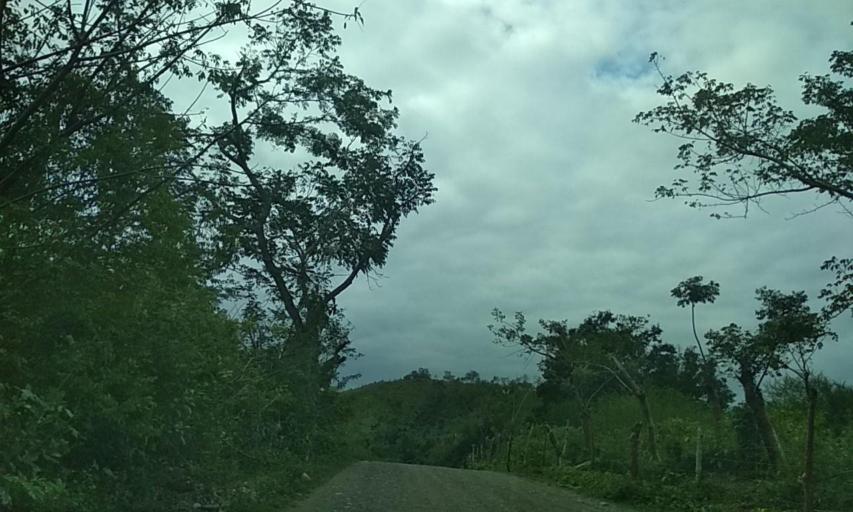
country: MX
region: Veracruz
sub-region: Papantla
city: Residencial Tajin
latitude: 20.6138
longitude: -97.3601
